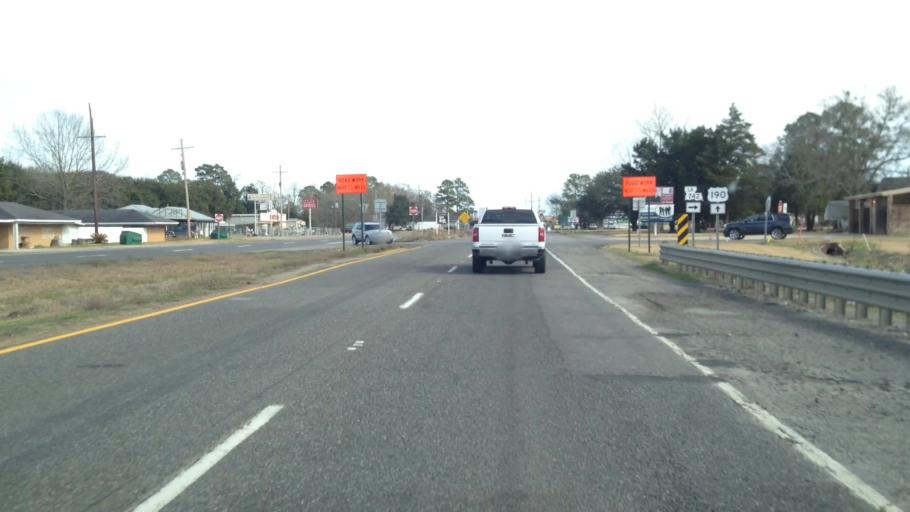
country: US
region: Louisiana
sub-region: Saint Landry Parish
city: Port Barre
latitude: 30.5469
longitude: -91.9717
